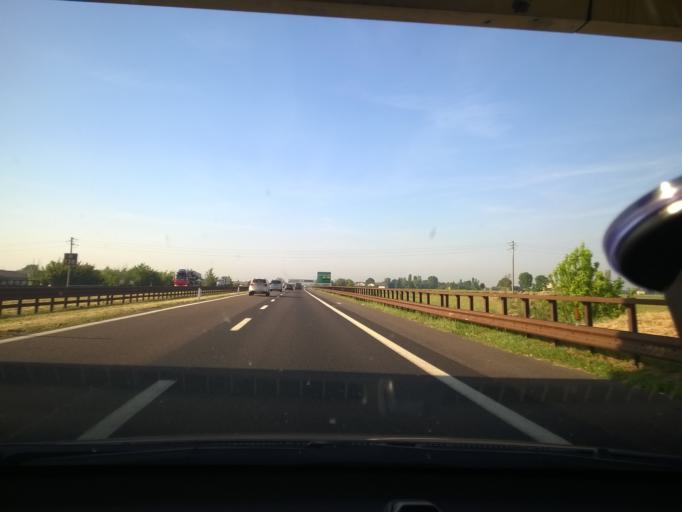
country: IT
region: Emilia-Romagna
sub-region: Provincia di Modena
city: Santa Croce Scuole
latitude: 44.7435
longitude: 10.8446
